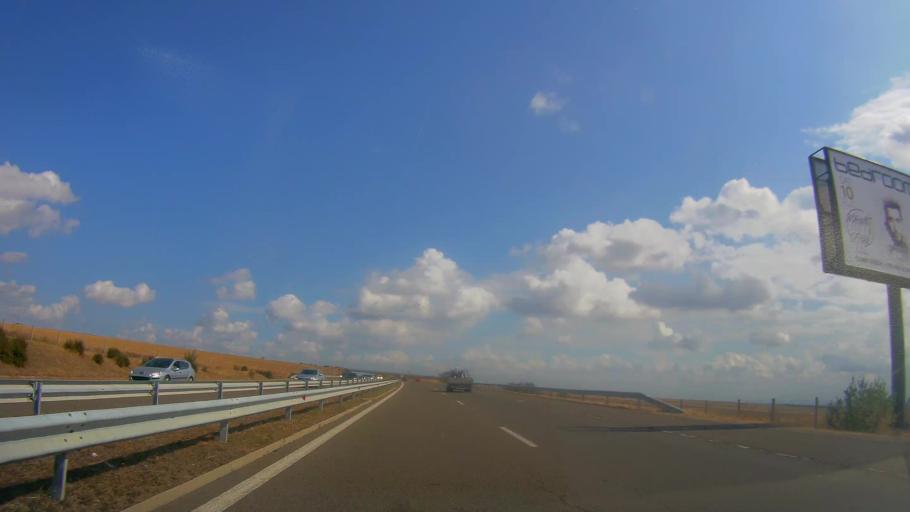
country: BG
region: Burgas
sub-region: Obshtina Kameno
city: Kameno
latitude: 42.5908
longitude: 27.1798
